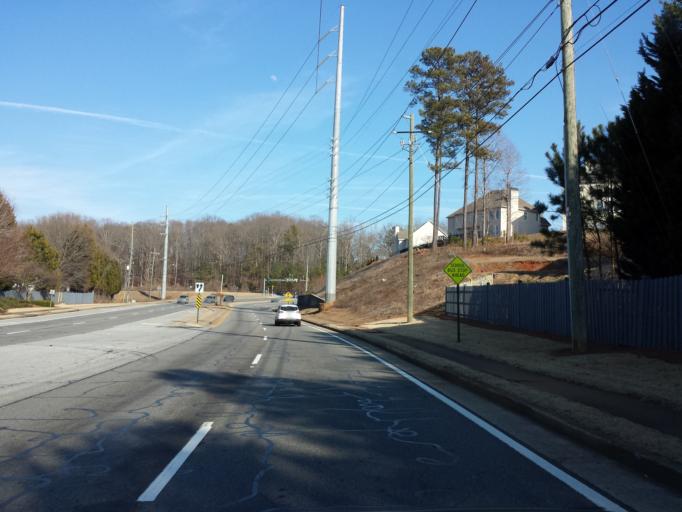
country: US
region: Georgia
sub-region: Cherokee County
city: Woodstock
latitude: 34.0355
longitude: -84.5348
